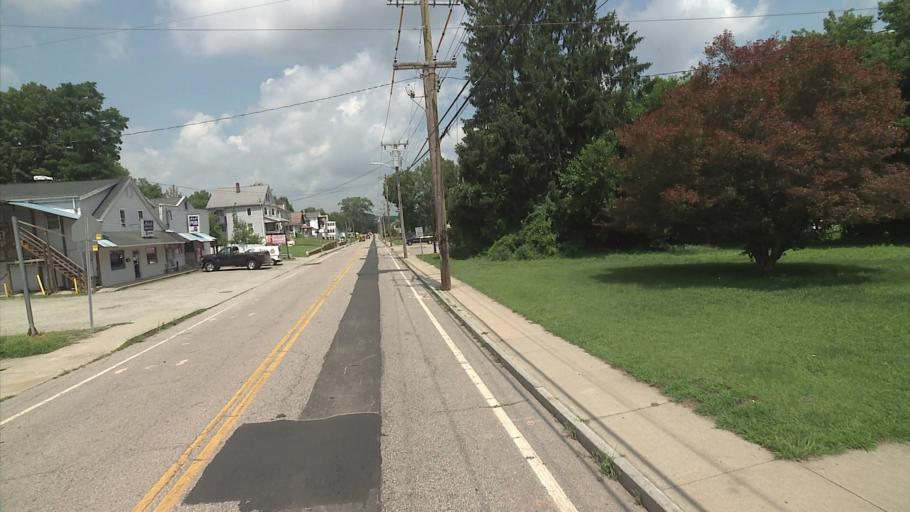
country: US
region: Connecticut
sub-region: New London County
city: Jewett City
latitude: 41.5993
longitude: -71.9801
